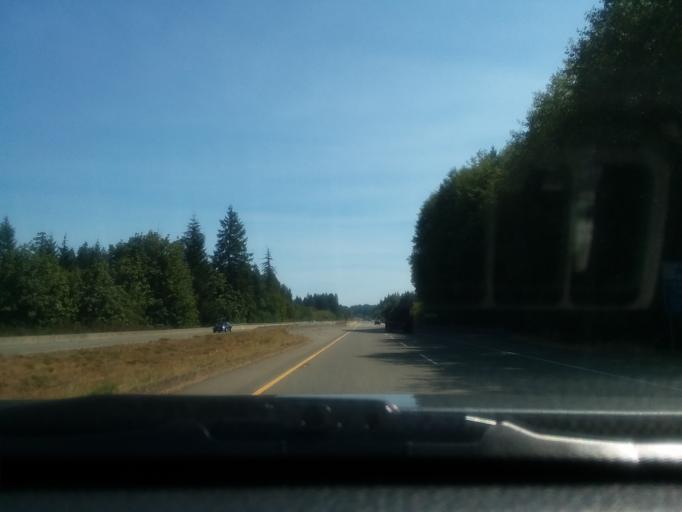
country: CA
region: British Columbia
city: Port Alberni
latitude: 49.4422
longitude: -124.7605
